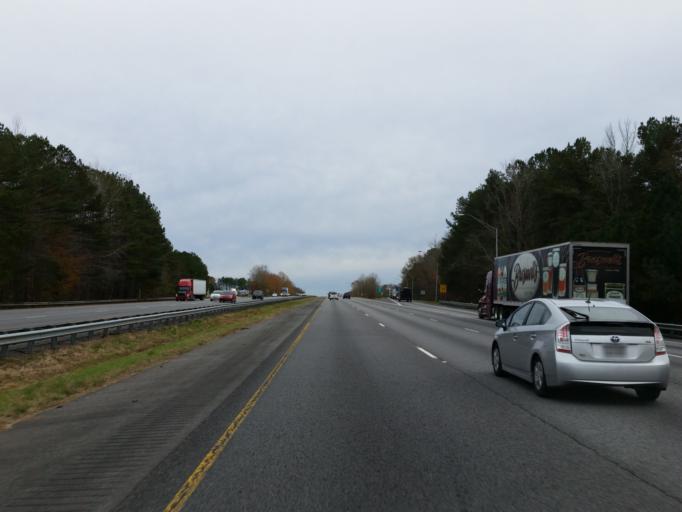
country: US
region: Georgia
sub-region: Monroe County
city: Forsyth
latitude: 33.0732
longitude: -83.9785
